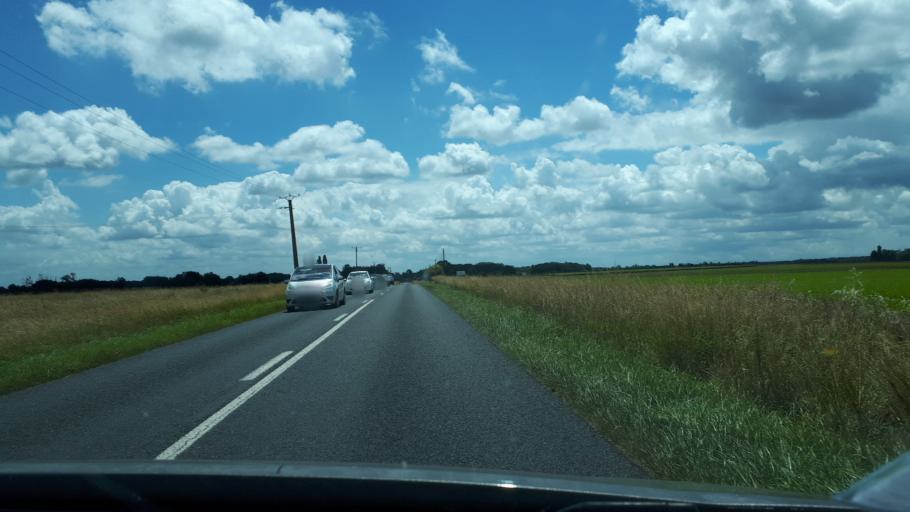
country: FR
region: Centre
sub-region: Departement du Loir-et-Cher
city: Contres
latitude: 47.3786
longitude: 1.4066
